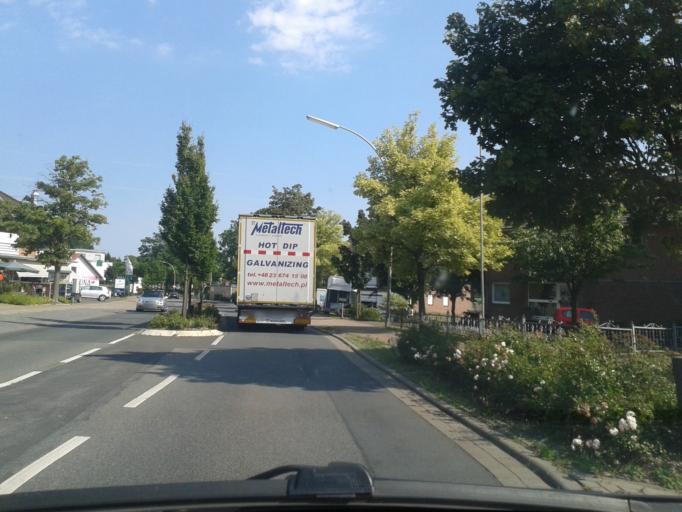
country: DE
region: North Rhine-Westphalia
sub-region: Regierungsbezirk Detmold
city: Verl
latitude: 51.8560
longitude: 8.5666
